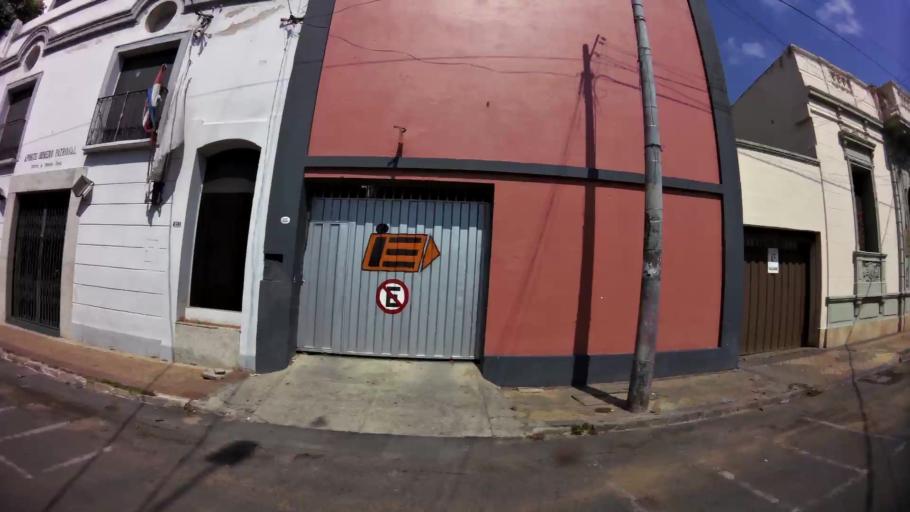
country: PY
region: Asuncion
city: Asuncion
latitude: -25.2867
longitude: -57.6373
